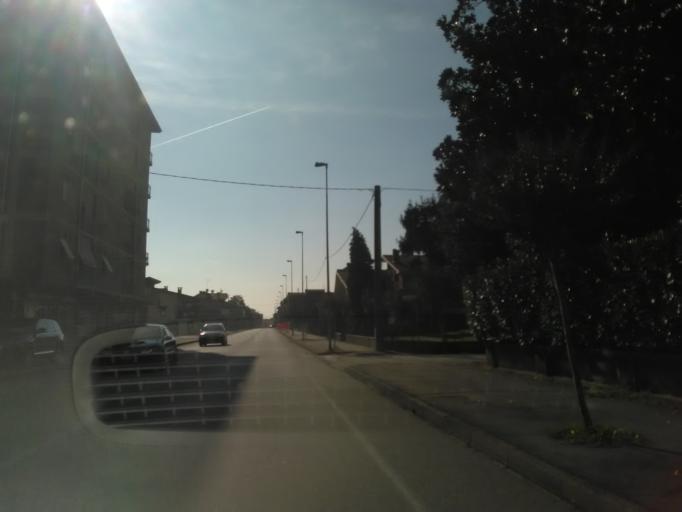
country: IT
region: Piedmont
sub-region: Provincia di Vercelli
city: Gattinara
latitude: 45.6238
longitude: 8.3714
